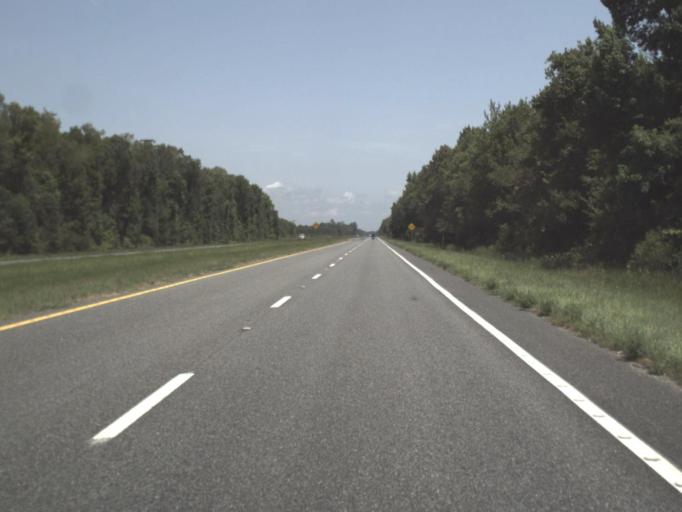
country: US
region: Florida
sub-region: Taylor County
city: Steinhatchee
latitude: 29.8370
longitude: -83.3672
